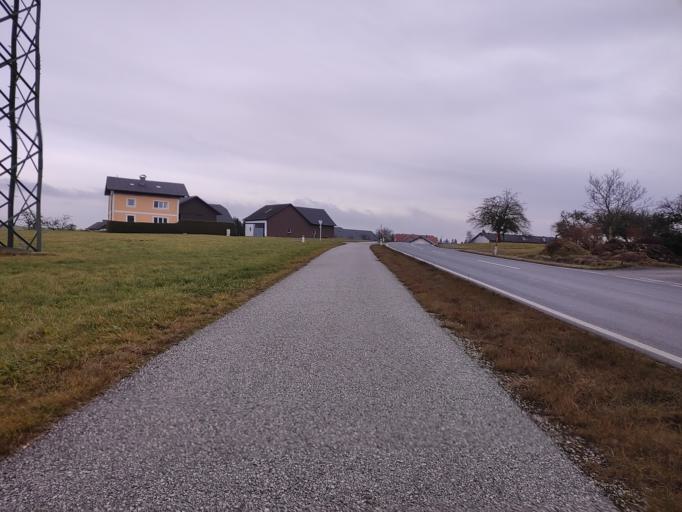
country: AT
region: Salzburg
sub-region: Politischer Bezirk Salzburg-Umgebung
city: Obertrum am See
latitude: 47.9215
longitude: 13.0973
